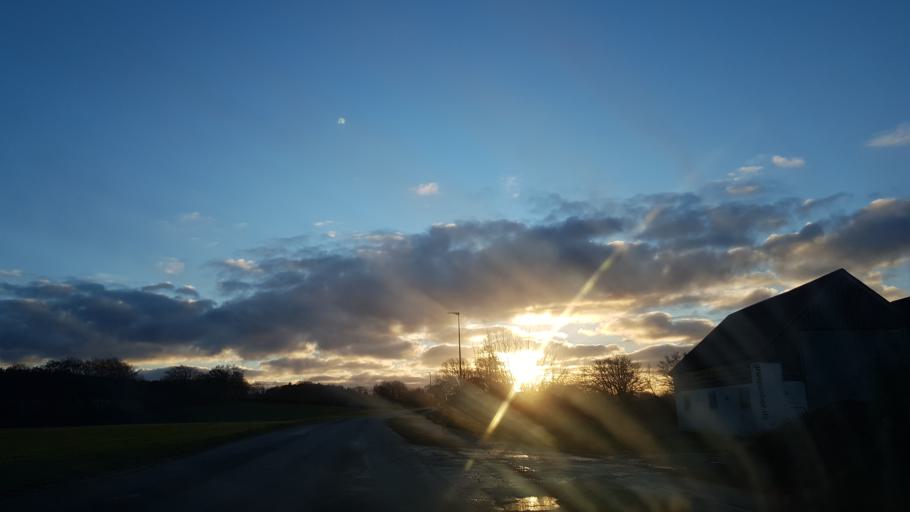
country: DK
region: South Denmark
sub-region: Kolding Kommune
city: Vamdrup
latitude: 55.3987
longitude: 9.3733
